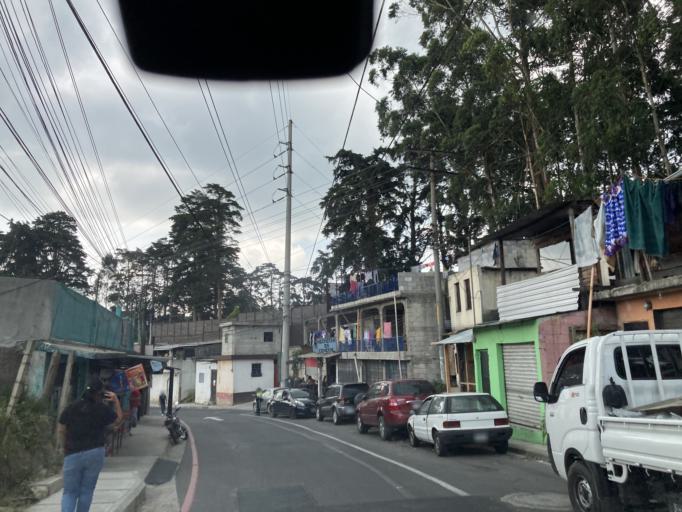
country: GT
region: Guatemala
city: Santa Catarina Pinula
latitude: 14.5561
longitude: -90.4568
